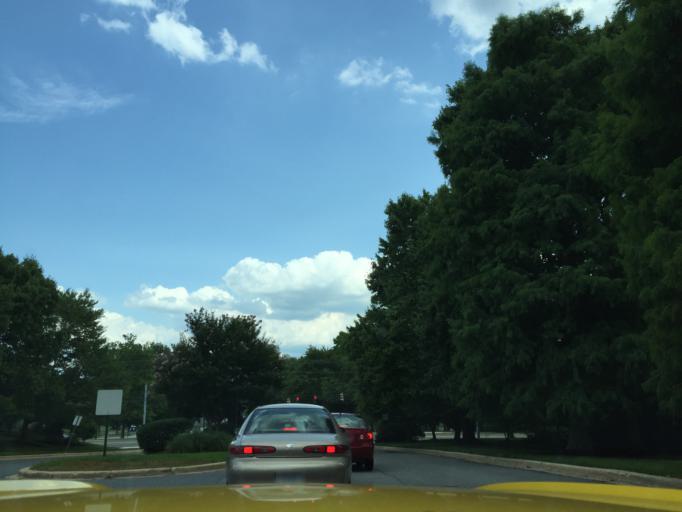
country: US
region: Delaware
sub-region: New Castle County
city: Bellefonte
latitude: 39.7998
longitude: -75.5244
